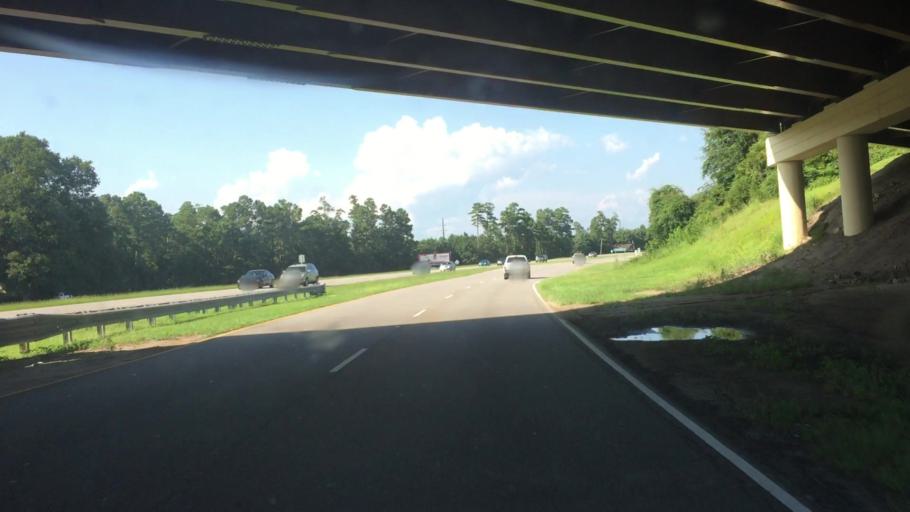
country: US
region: South Carolina
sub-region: Horry County
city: Myrtle Beach
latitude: 33.7675
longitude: -78.8050
